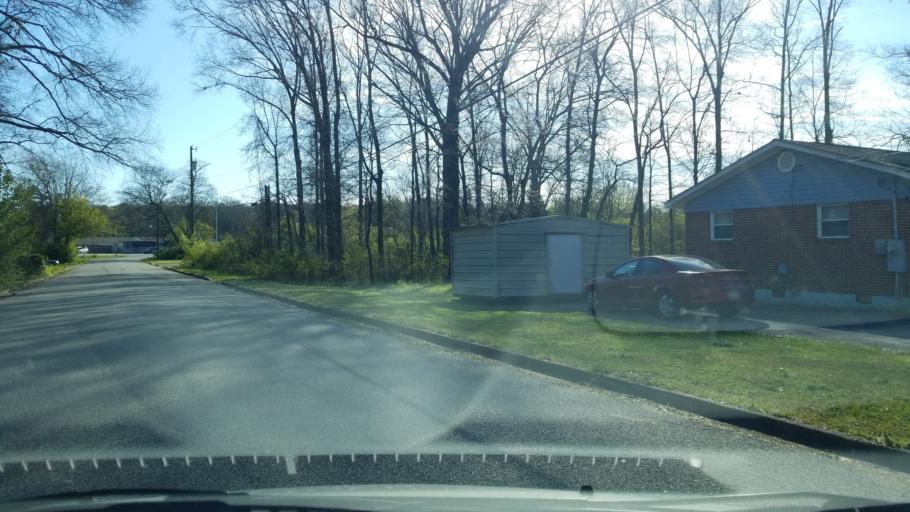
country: US
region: Tennessee
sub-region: Hamilton County
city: East Brainerd
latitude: 35.0399
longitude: -85.1908
